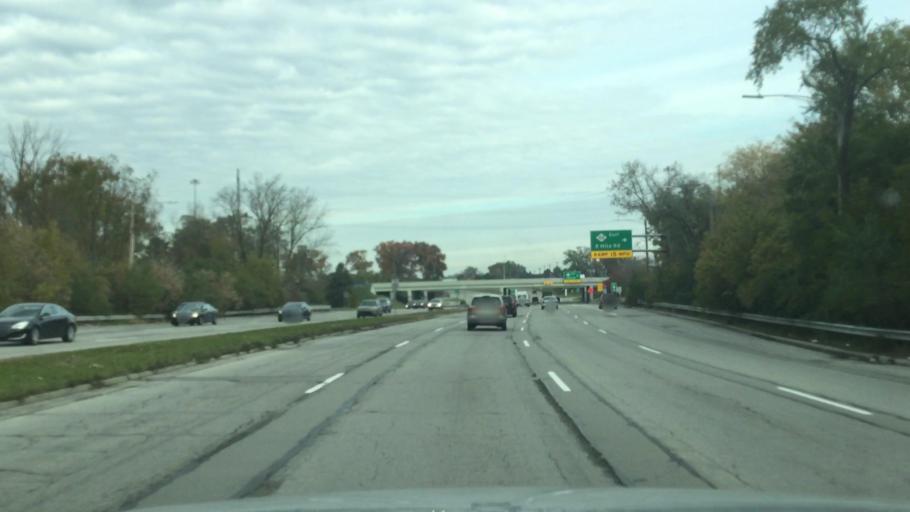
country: US
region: Michigan
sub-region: Wayne County
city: Redford
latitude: 42.4404
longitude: -83.2789
